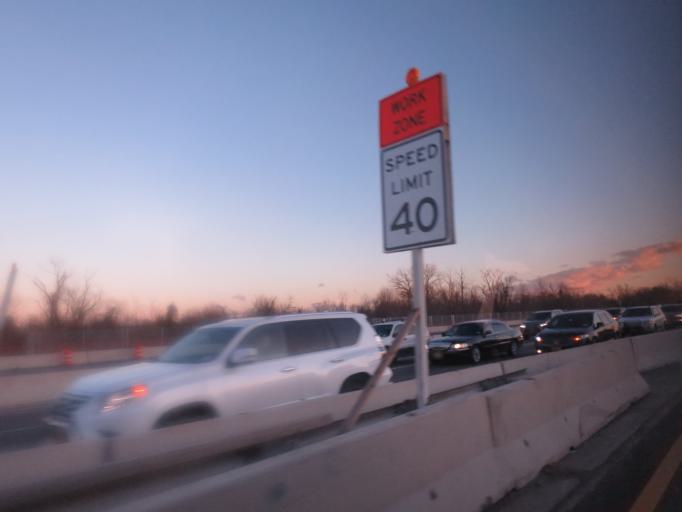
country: US
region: New York
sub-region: Kings County
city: East New York
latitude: 40.6125
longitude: -73.8971
